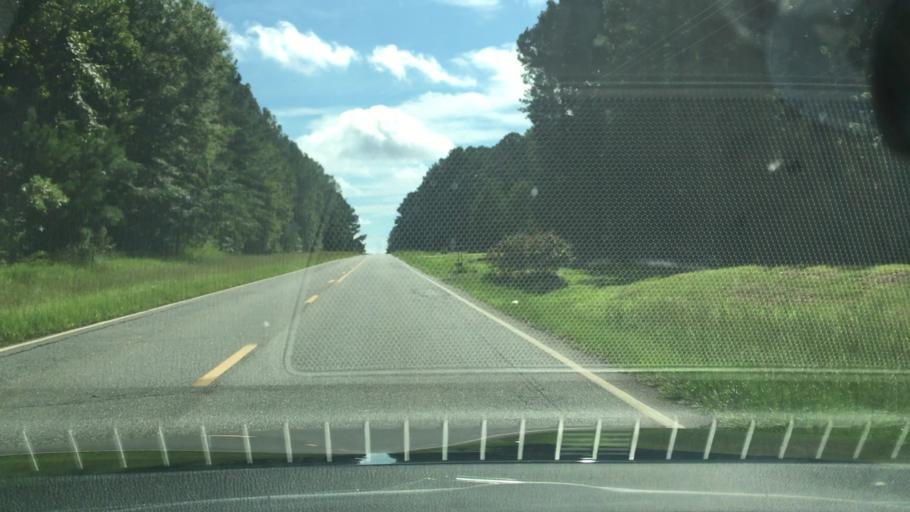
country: US
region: Georgia
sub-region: Putnam County
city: Jefferson
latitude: 33.4478
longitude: -83.3189
